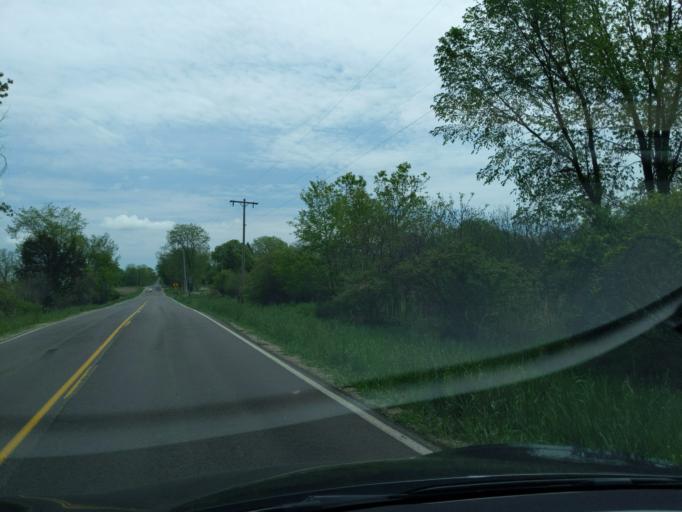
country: US
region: Michigan
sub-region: Ingham County
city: Stockbridge
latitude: 42.4684
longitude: -84.1638
